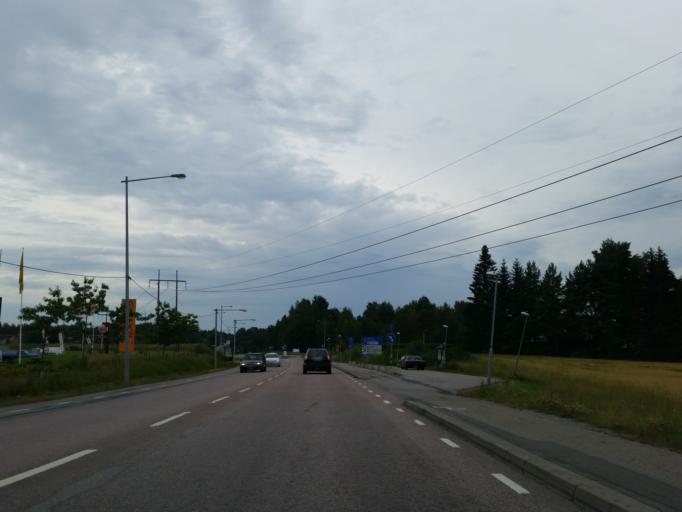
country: SE
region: Stockholm
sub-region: Nykvarns Kommun
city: Nykvarn
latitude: 59.1889
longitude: 17.4584
